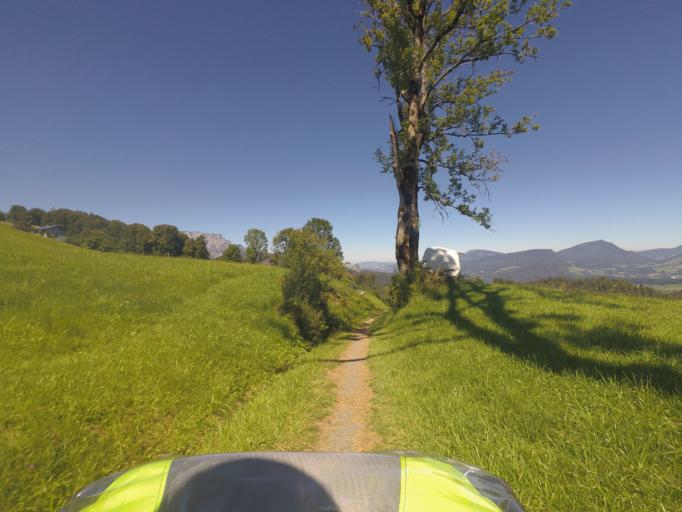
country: AT
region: Salzburg
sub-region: Politischer Bezirk Hallein
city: Hallein
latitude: 47.6590
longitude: 13.0901
